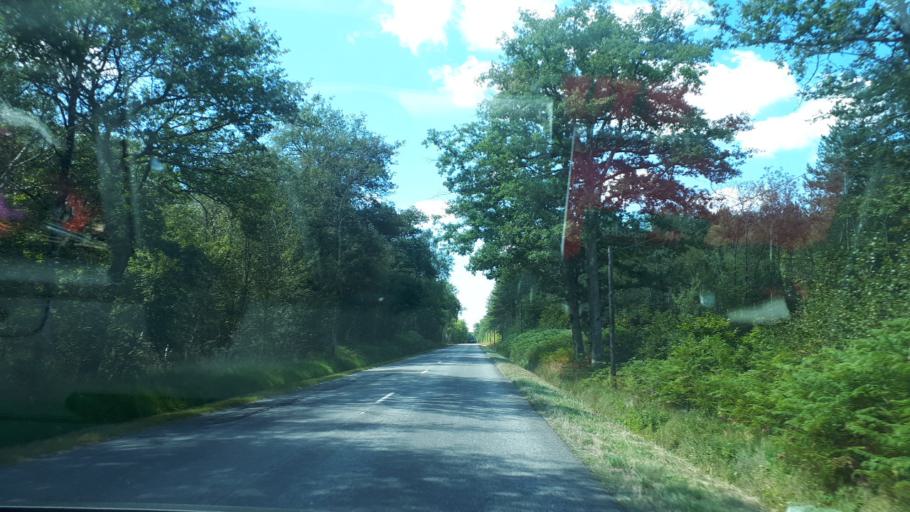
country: FR
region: Centre
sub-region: Departement du Loir-et-Cher
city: Chaumont-sur-Tharonne
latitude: 47.5700
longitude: 1.9164
